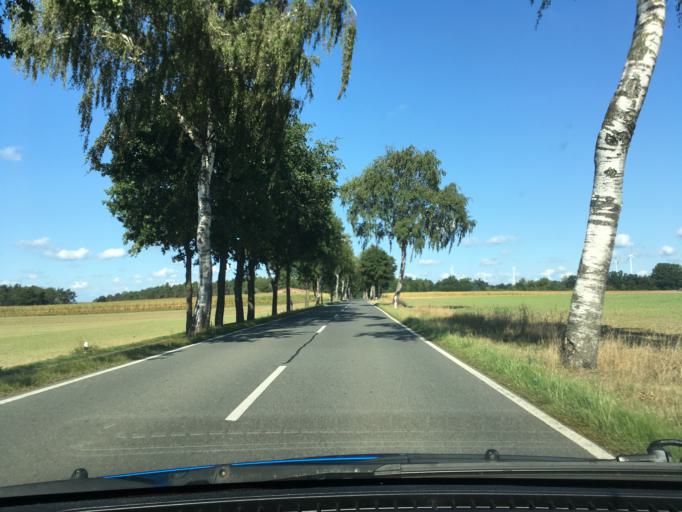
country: DE
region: Lower Saxony
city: Hermannsburg
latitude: 52.8539
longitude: 10.0599
